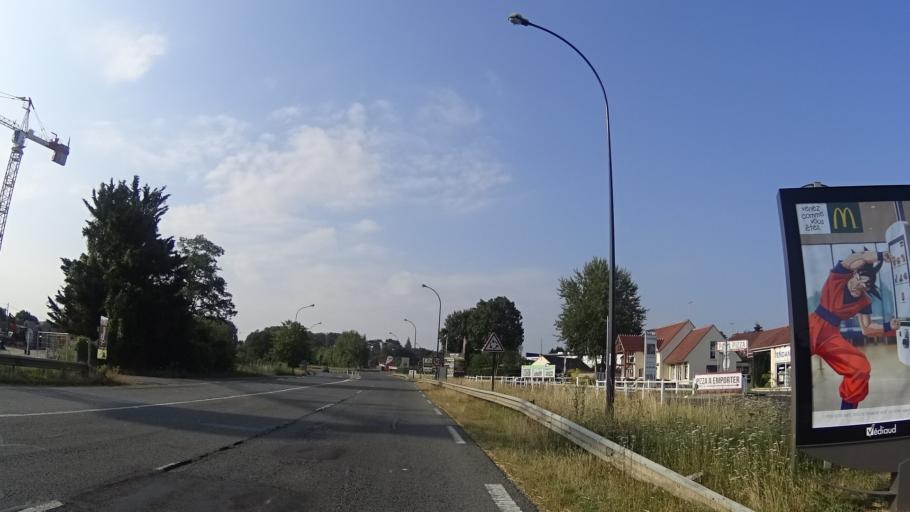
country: FR
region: Ile-de-France
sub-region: Departement du Val-d'Oise
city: Chaumontel
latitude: 49.1210
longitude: 2.4268
